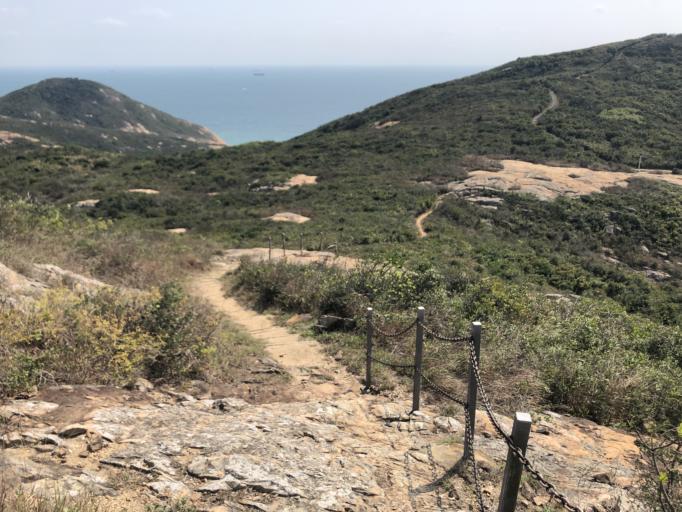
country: HK
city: Sok Kwu Wan
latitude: 22.1681
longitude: 114.2605
